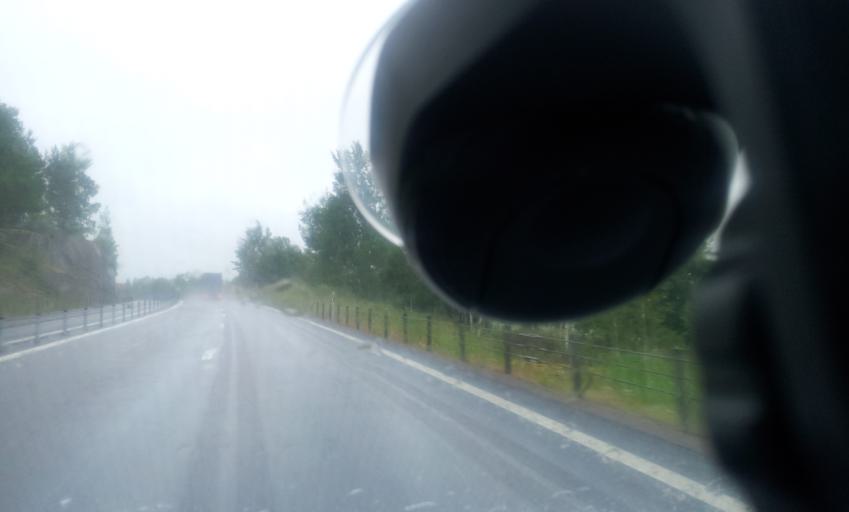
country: SE
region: OEstergoetland
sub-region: Soderkopings Kommun
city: Soederkoeping
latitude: 58.3923
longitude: 16.4107
